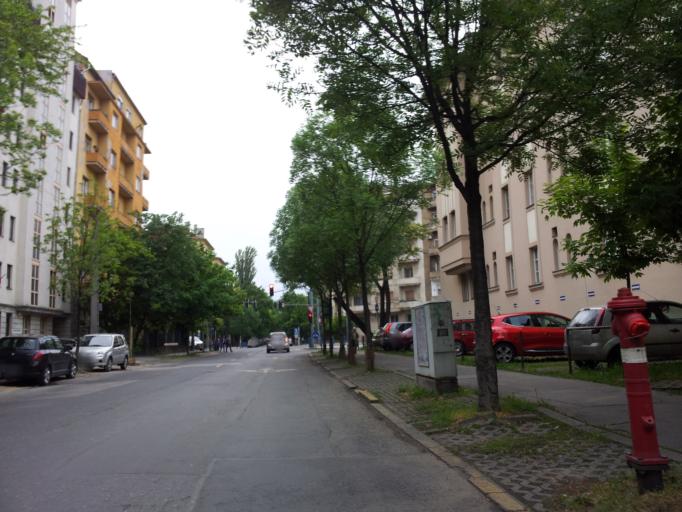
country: HU
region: Budapest
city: Budapest XI. keruelet
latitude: 47.4745
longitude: 19.0397
